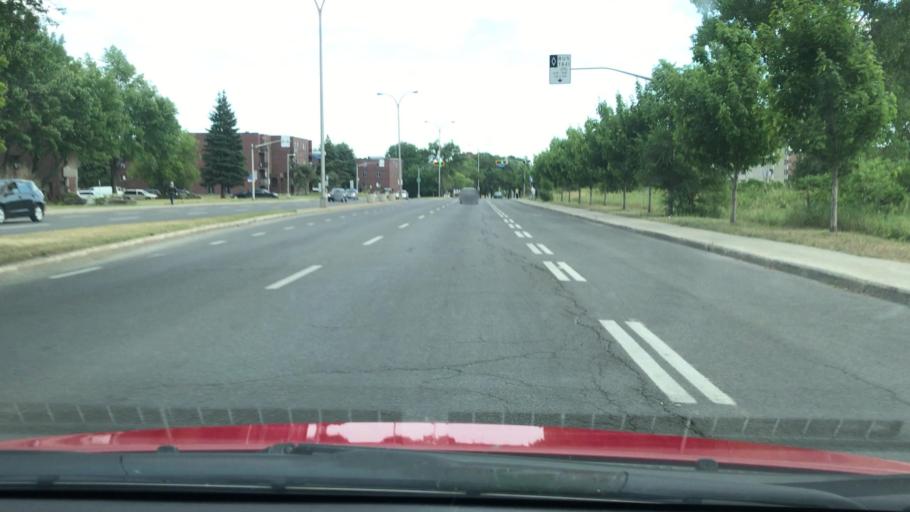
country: CA
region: Quebec
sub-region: Laval
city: Laval
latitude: 45.5481
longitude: -73.7424
